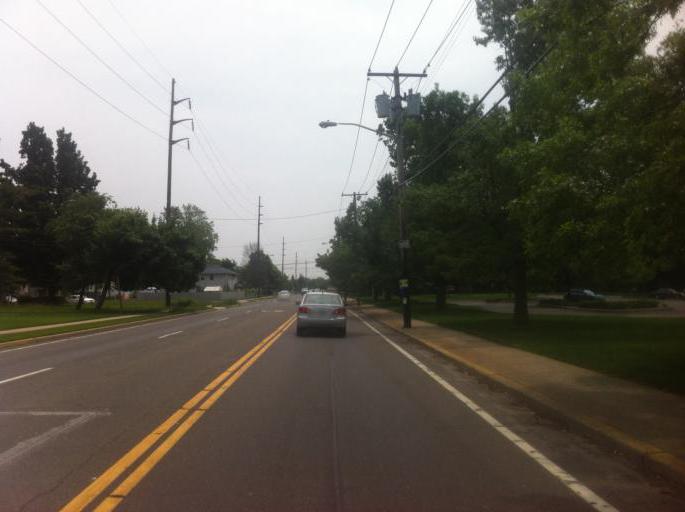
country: US
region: New York
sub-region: Nassau County
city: Plainedge
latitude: 40.7228
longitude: -73.4869
